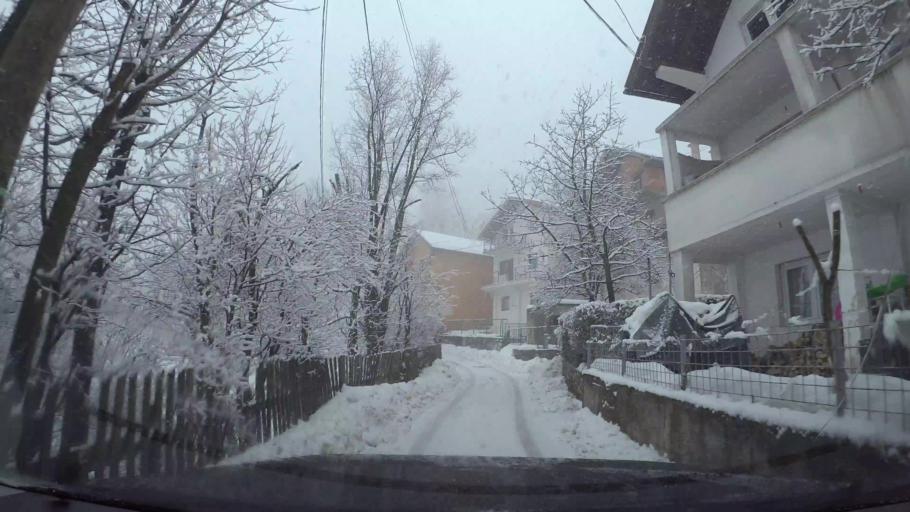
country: BA
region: Federation of Bosnia and Herzegovina
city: Kobilja Glava
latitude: 43.8498
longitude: 18.4555
